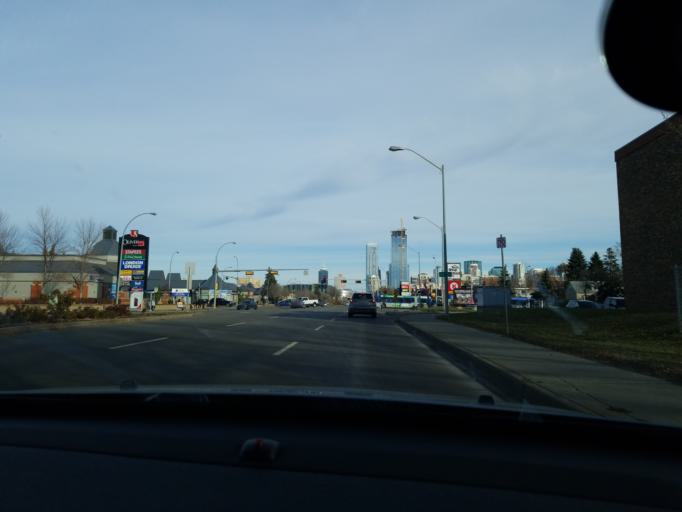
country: CA
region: Alberta
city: Edmonton
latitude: 53.5462
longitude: -113.5230
